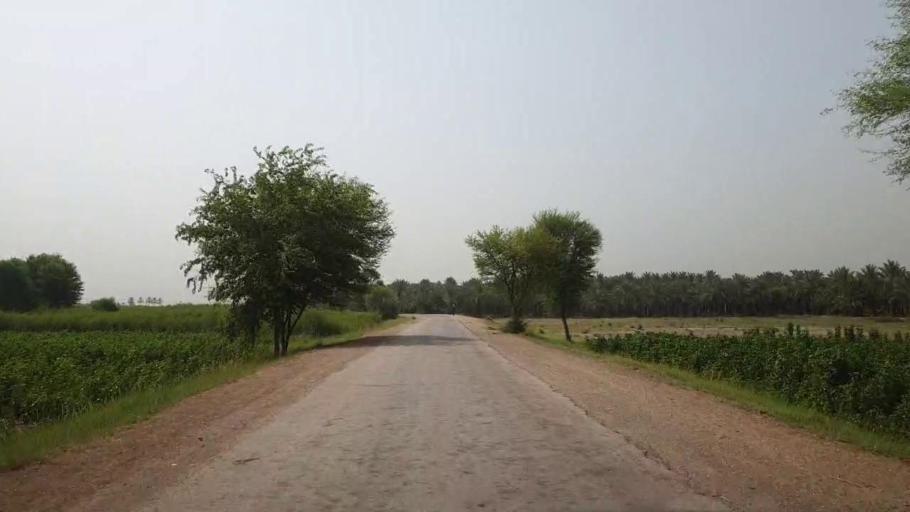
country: PK
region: Sindh
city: Gambat
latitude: 27.4308
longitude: 68.5344
